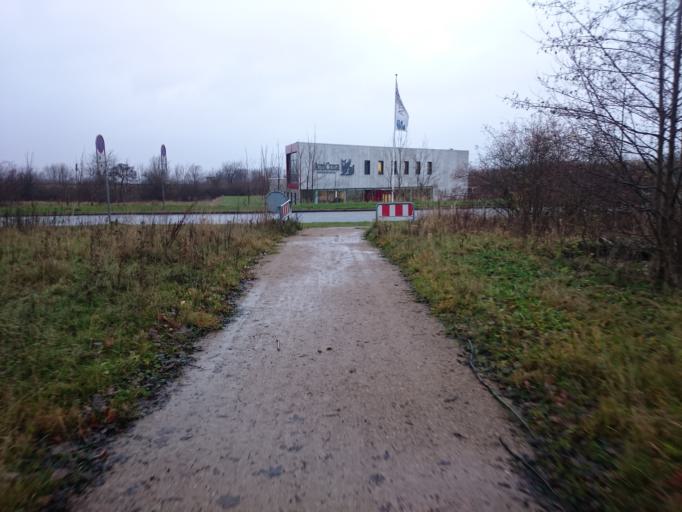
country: DK
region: Central Jutland
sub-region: Arhus Kommune
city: Stavtrup
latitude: 56.1162
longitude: 10.1299
